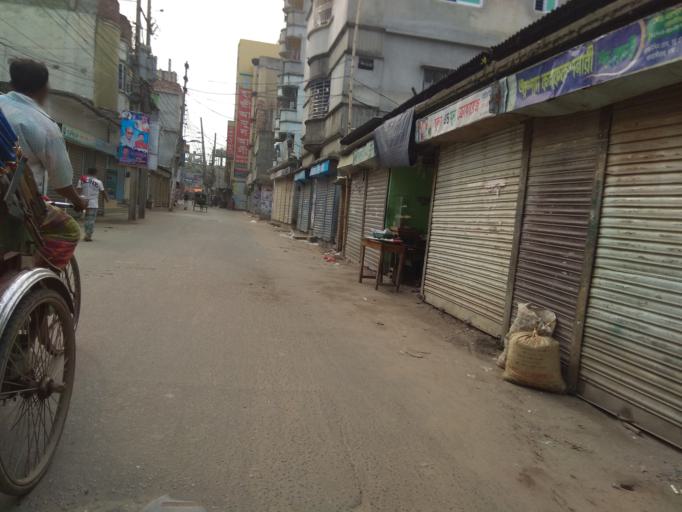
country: BD
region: Dhaka
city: Azimpur
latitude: 23.7165
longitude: 90.3714
